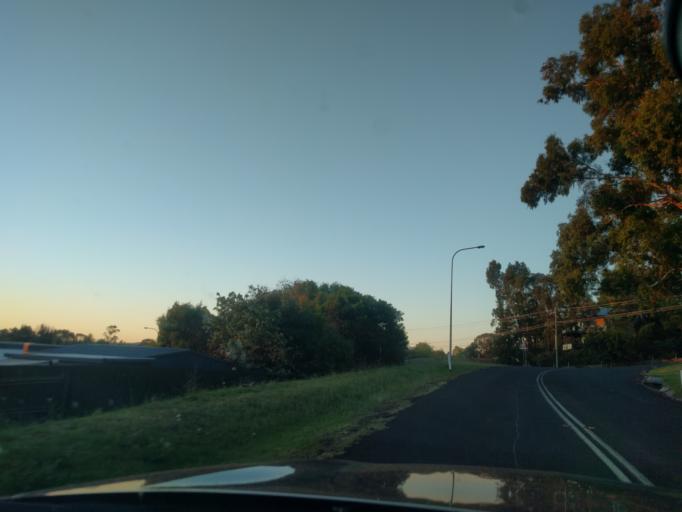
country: AU
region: New South Wales
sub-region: Armidale Dumaresq
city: Armidale
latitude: -30.5006
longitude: 151.6616
